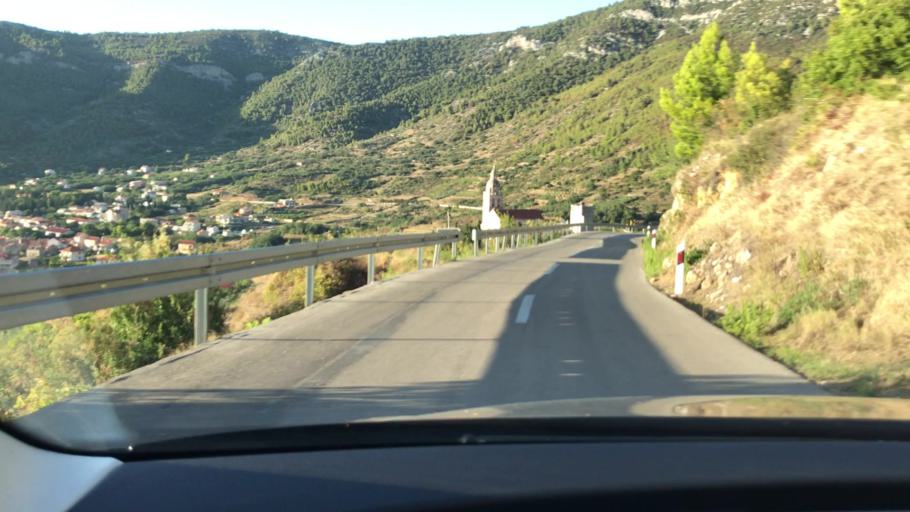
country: HR
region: Splitsko-Dalmatinska
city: Komiza
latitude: 43.0380
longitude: 16.0956
